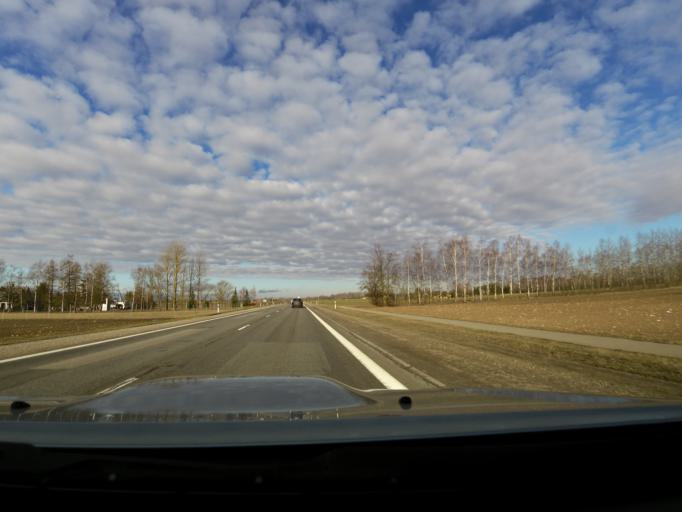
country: LT
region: Panevezys
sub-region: Panevezys City
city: Panevezys
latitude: 55.7370
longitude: 24.2048
